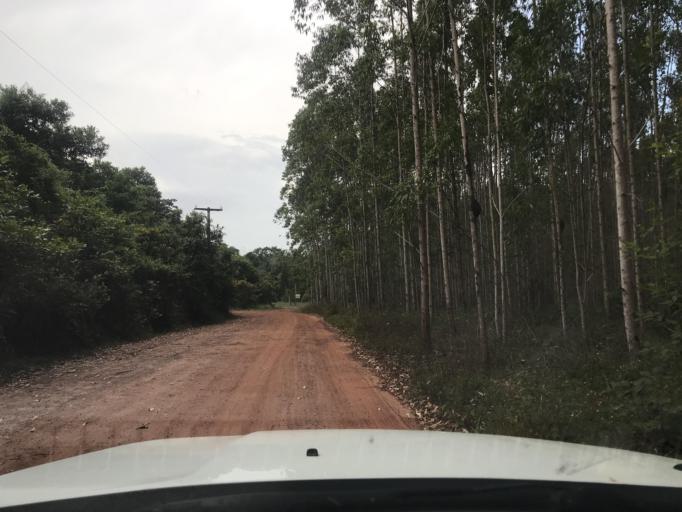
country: BR
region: Bahia
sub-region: Entre Rios
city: Entre Rios
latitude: -12.1147
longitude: -38.1802
